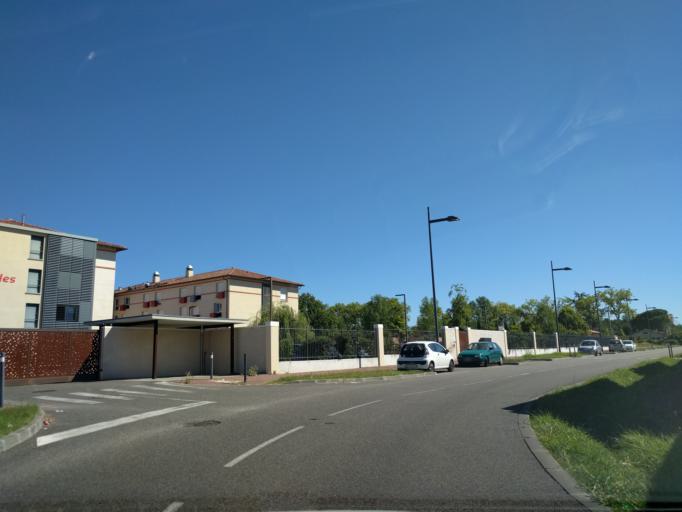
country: FR
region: Midi-Pyrenees
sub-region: Departement du Tarn-et-Garonne
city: Montauban
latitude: 44.0400
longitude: 1.3543
